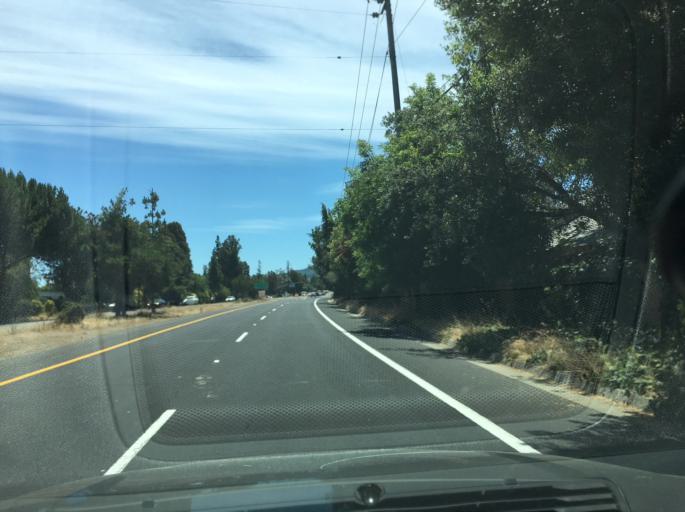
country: US
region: California
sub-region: Santa Clara County
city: Seven Trees
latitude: 37.2115
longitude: -121.8485
